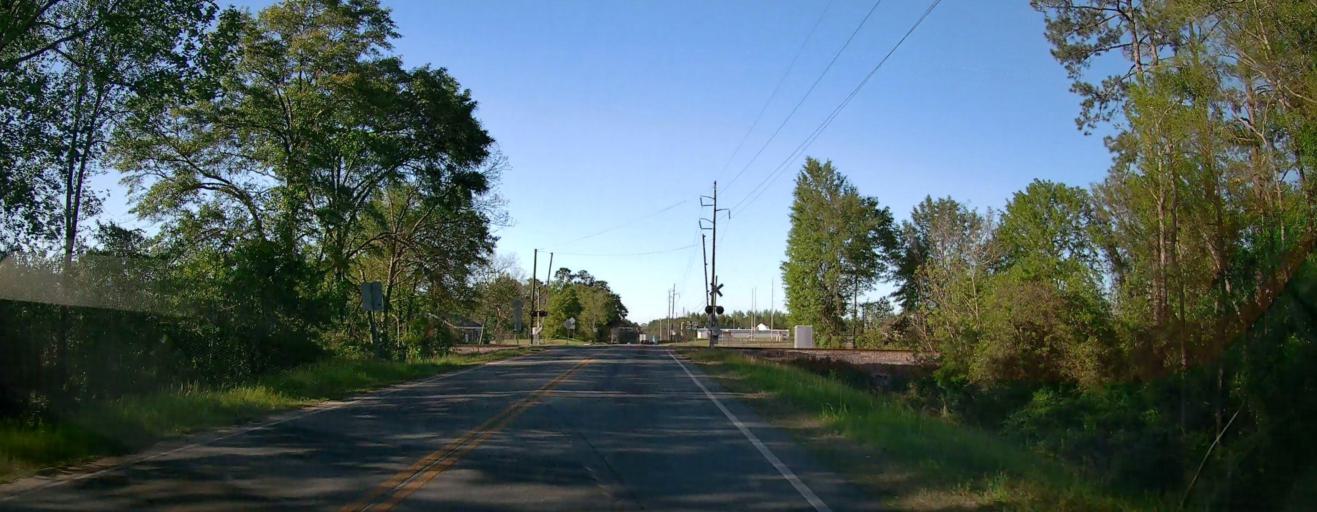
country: US
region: Georgia
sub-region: Ben Hill County
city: Fitzgerald
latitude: 31.7109
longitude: -83.2357
